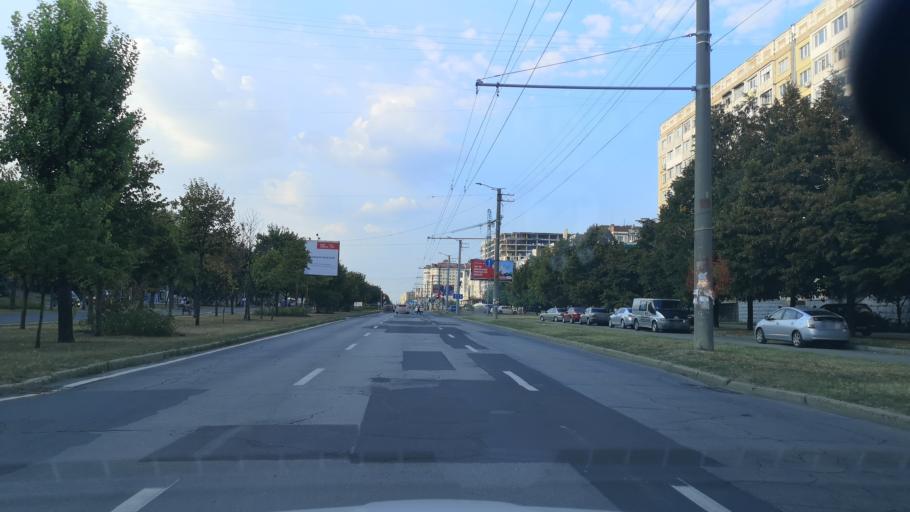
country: MD
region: Chisinau
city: Chisinau
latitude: 47.0417
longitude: 28.8904
